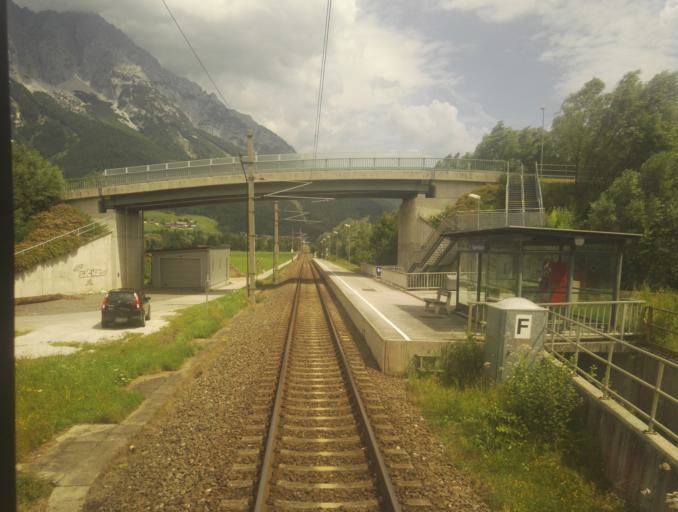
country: AT
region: Styria
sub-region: Politischer Bezirk Liezen
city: Niederoblarn
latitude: 47.4814
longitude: 14.0139
